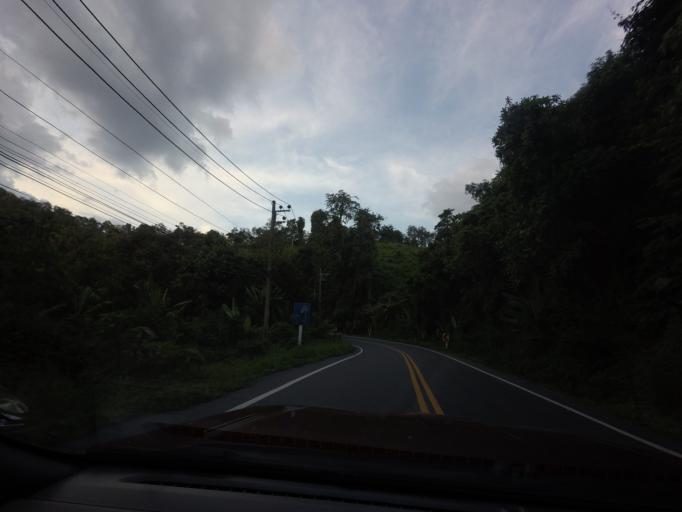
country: TH
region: Yala
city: Than To
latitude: 6.0367
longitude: 101.2049
